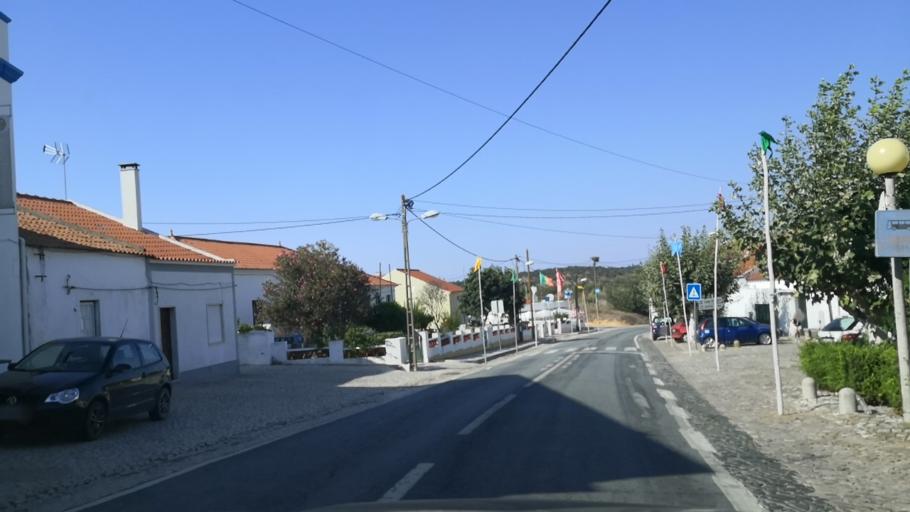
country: PT
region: Santarem
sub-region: Benavente
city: Poceirao
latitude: 38.7679
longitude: -8.6263
